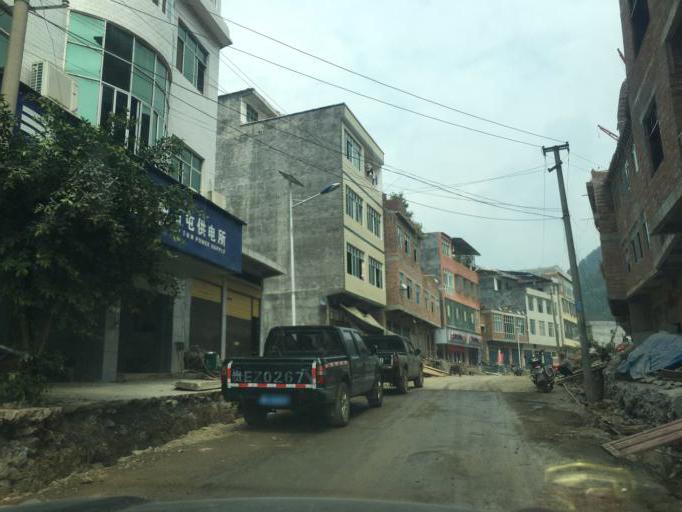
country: CN
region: Guangxi Zhuangzu Zizhiqu
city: Tongle
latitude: 25.3299
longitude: 105.9882
